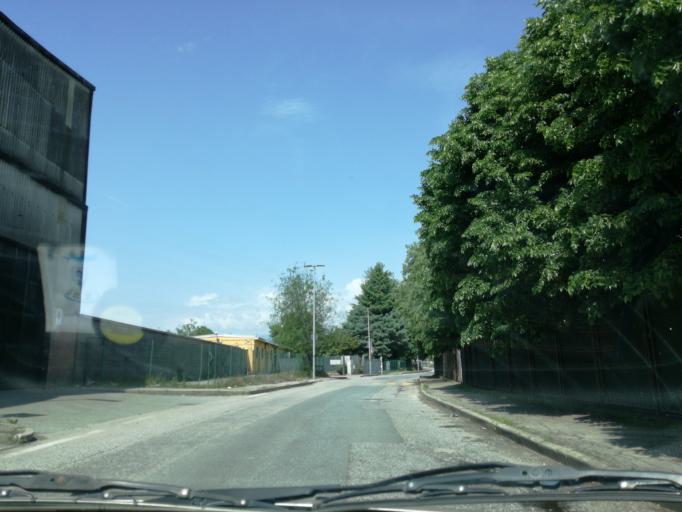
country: IT
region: Piedmont
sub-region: Provincia di Torino
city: Savonera
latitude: 45.0872
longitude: 7.6248
